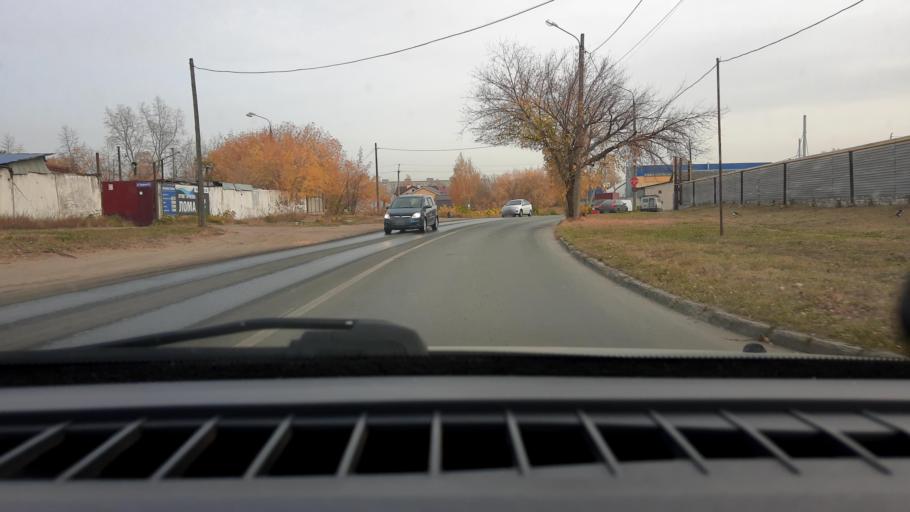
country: RU
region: Nizjnij Novgorod
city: Gorbatovka
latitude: 56.3463
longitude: 43.8229
